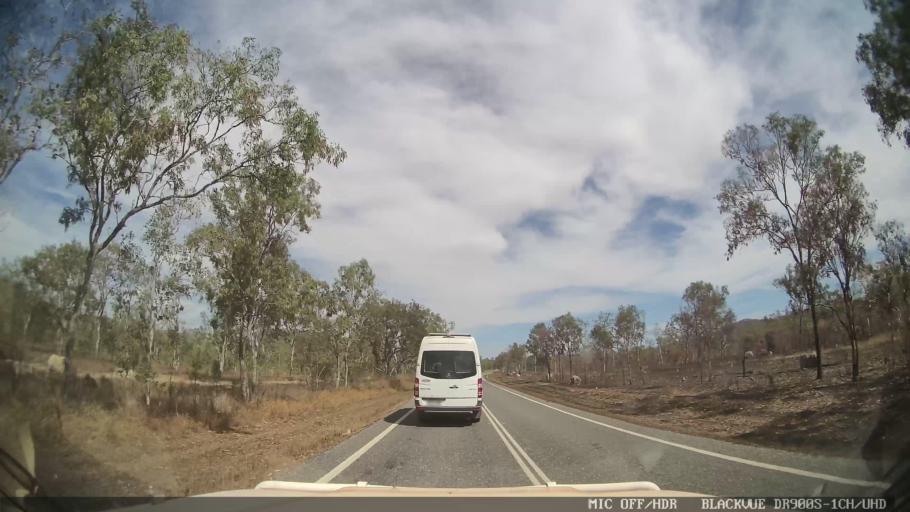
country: AU
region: Queensland
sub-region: Cairns
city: Port Douglas
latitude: -16.7216
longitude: 145.3530
